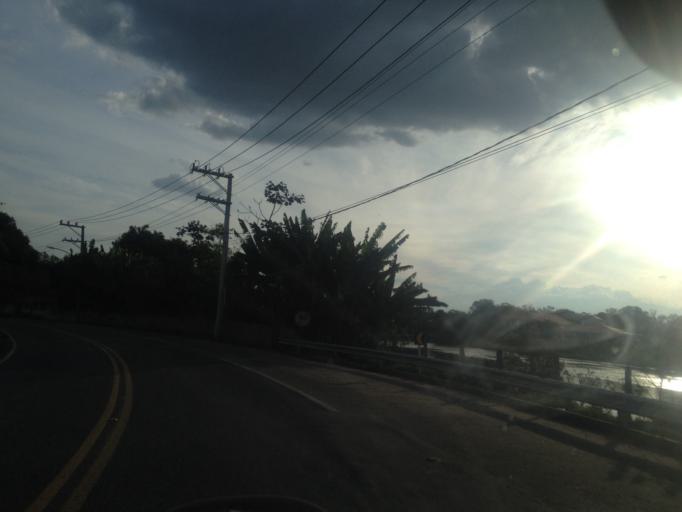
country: BR
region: Rio de Janeiro
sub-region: Porto Real
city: Porto Real
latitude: -22.4236
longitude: -44.2814
